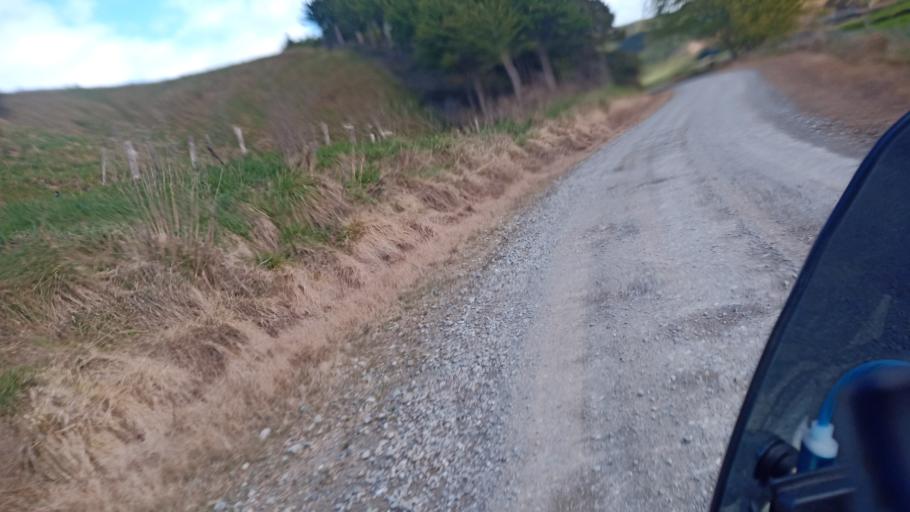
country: NZ
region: Gisborne
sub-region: Gisborne District
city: Gisborne
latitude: -38.3854
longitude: 178.2631
